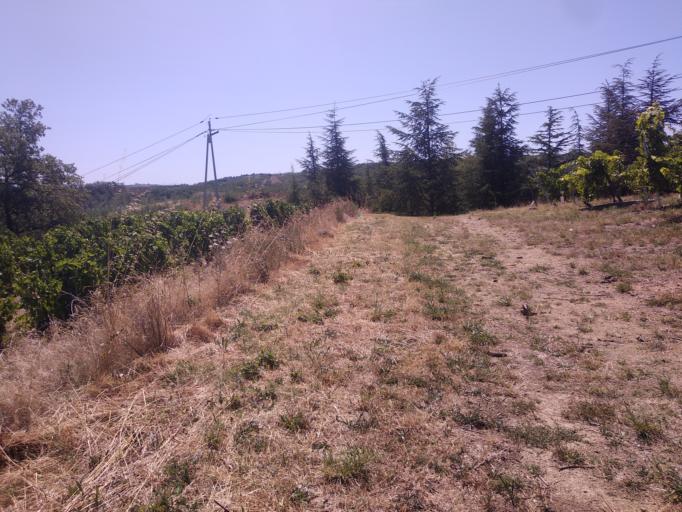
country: FR
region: Rhone-Alpes
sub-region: Departement de l'Ardeche
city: Sarras
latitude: 45.1848
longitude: 4.7866
